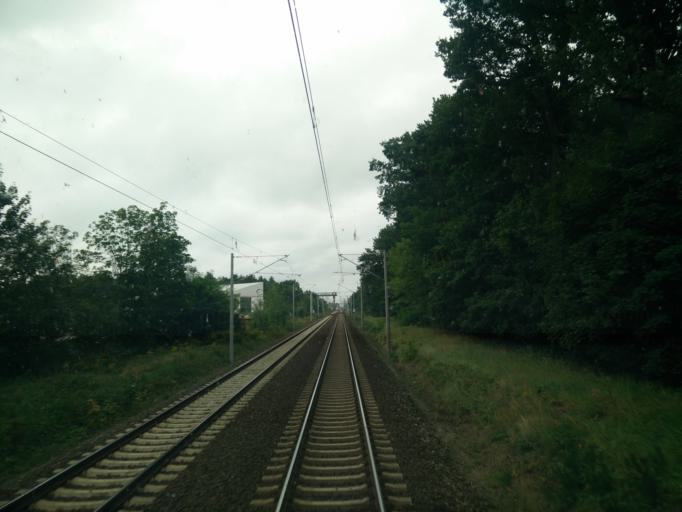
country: DE
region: Brandenburg
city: Luebben
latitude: 51.9473
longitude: 13.8653
